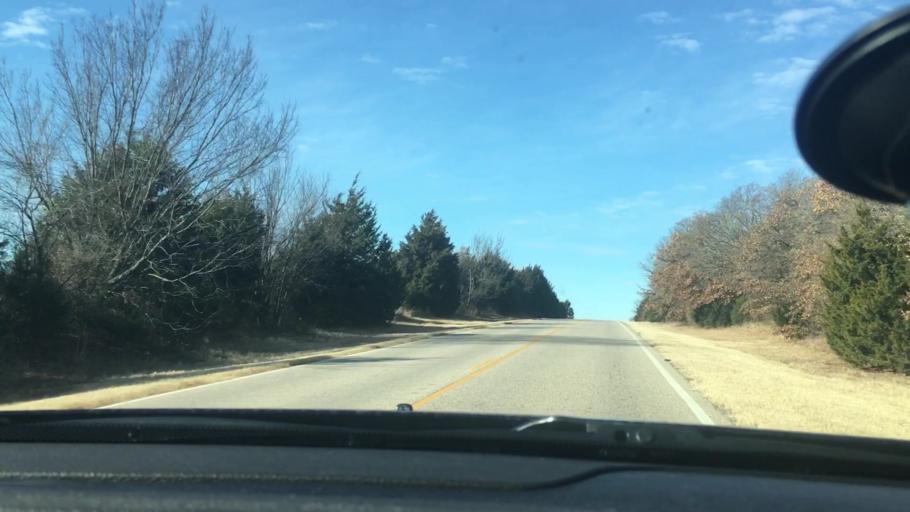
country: US
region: Oklahoma
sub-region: Garvin County
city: Stratford
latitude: 34.9860
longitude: -96.9712
